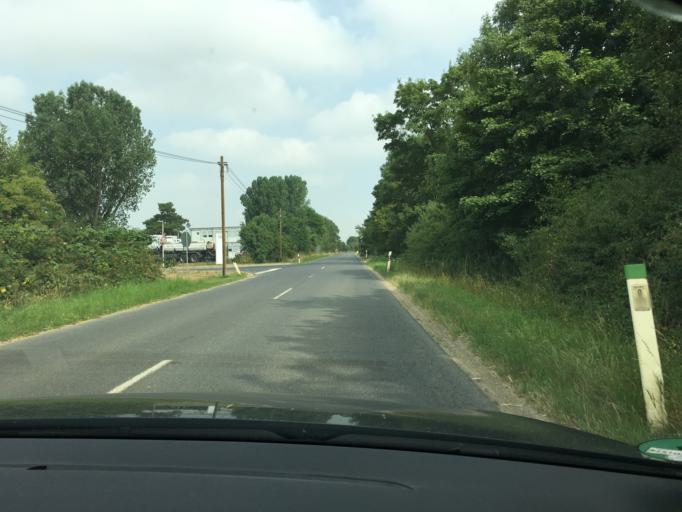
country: DE
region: North Rhine-Westphalia
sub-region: Regierungsbezirk Koln
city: Merzenich
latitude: 50.8181
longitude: 6.5878
